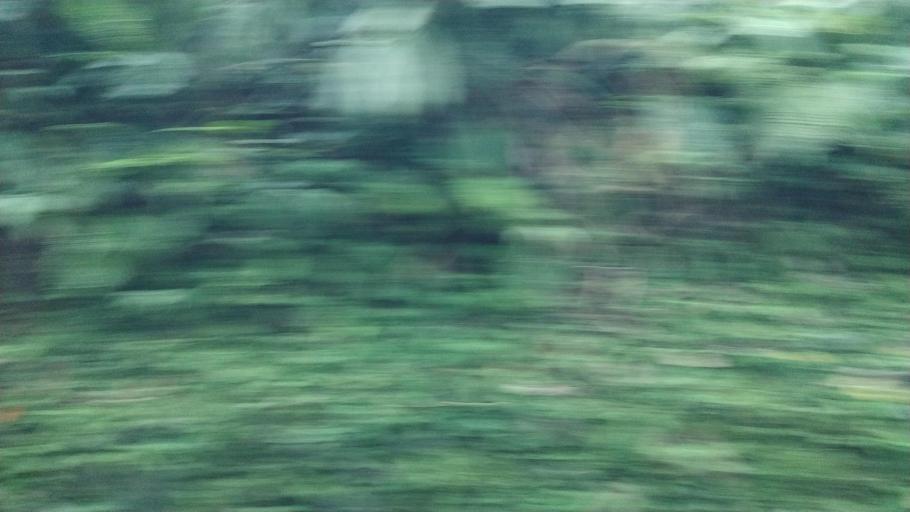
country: TW
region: Taiwan
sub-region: Hualien
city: Hualian
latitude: 23.9194
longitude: 121.5021
